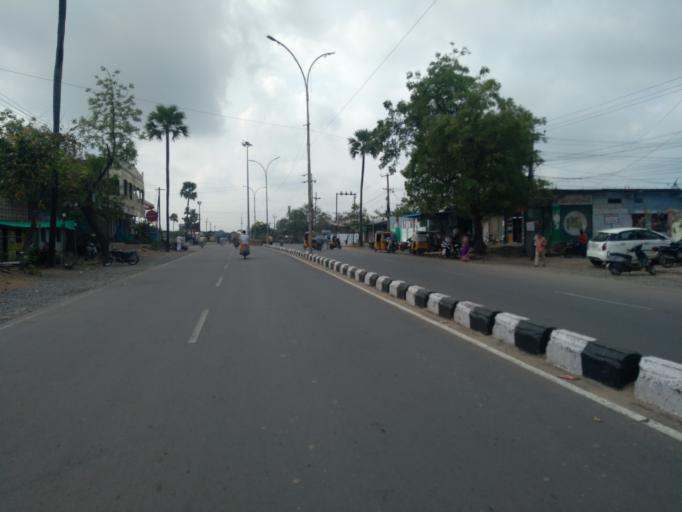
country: IN
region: Telangana
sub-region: Warangal
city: Warangal
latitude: 17.9610
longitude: 79.6008
